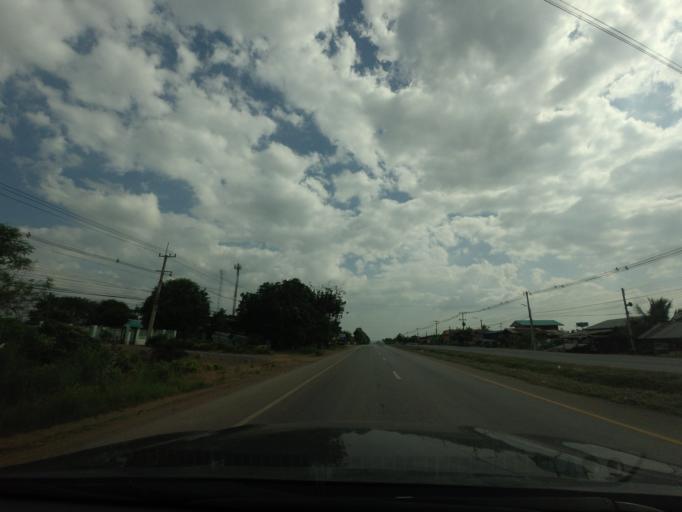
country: TH
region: Lop Buri
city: Chai Badan
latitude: 15.2522
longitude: 101.1255
